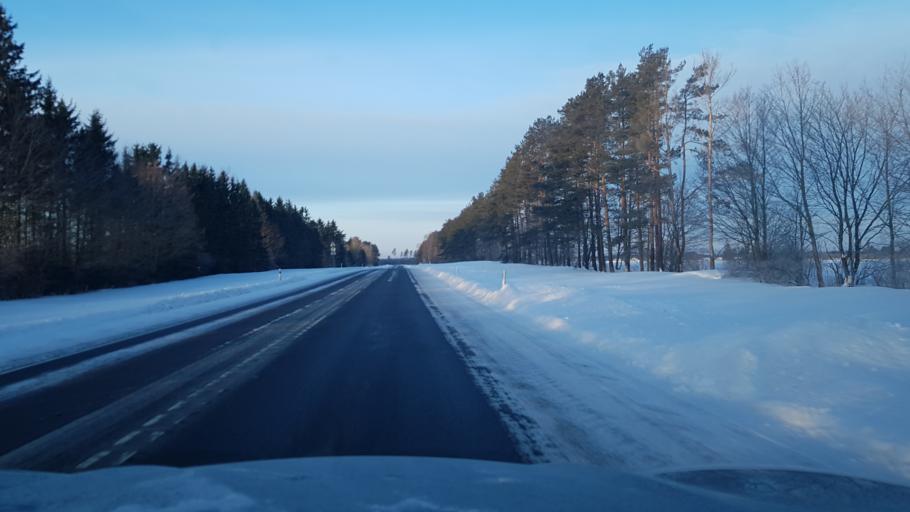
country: EE
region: Ida-Virumaa
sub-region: Toila vald
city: Voka
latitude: 59.3931
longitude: 27.6171
